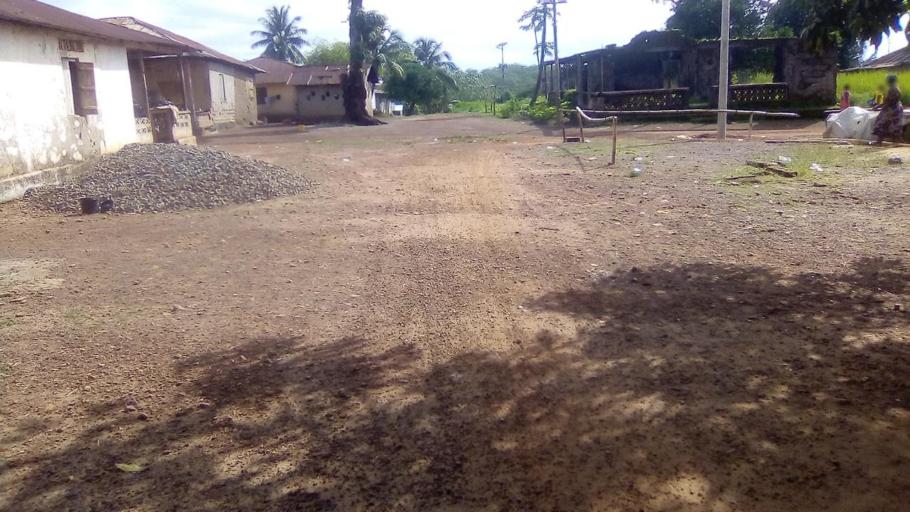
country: SL
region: Southern Province
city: Pujehun
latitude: 7.3579
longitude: -11.7200
